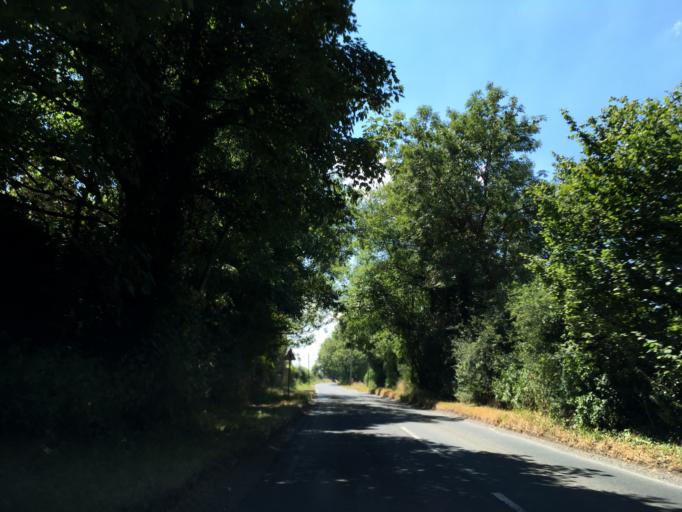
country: GB
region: England
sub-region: Gloucestershire
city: Chalford
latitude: 51.7426
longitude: -2.1457
